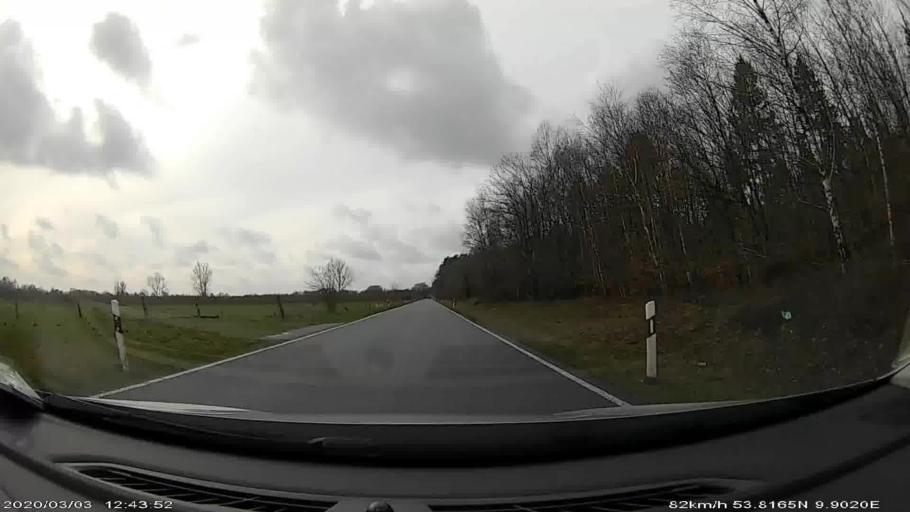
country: DE
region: Schleswig-Holstein
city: Alveslohe
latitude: 53.8153
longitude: 9.8991
